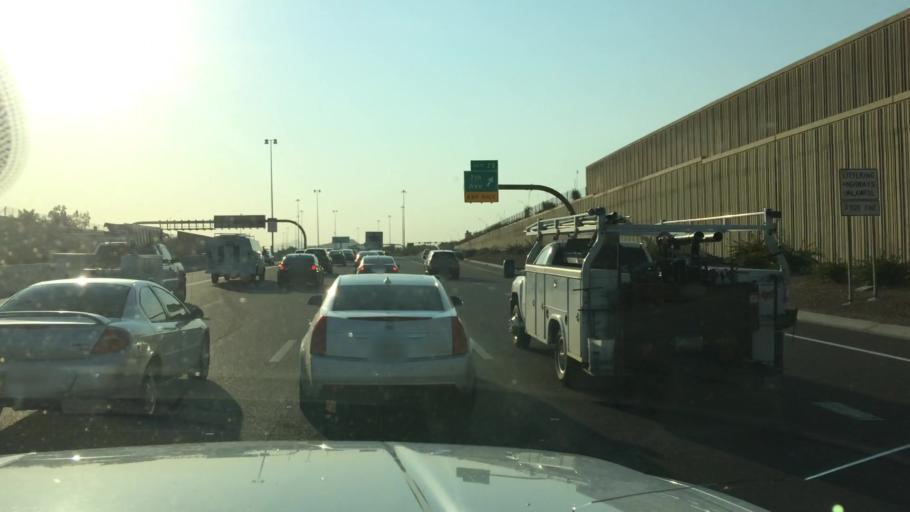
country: US
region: Arizona
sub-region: Maricopa County
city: Glendale
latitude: 33.6700
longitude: -112.0898
